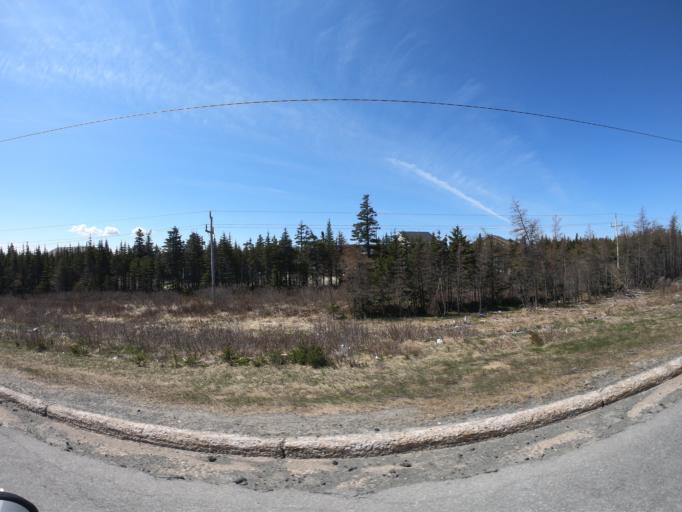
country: CA
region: Newfoundland and Labrador
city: Mount Pearl
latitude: 47.4996
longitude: -52.8134
